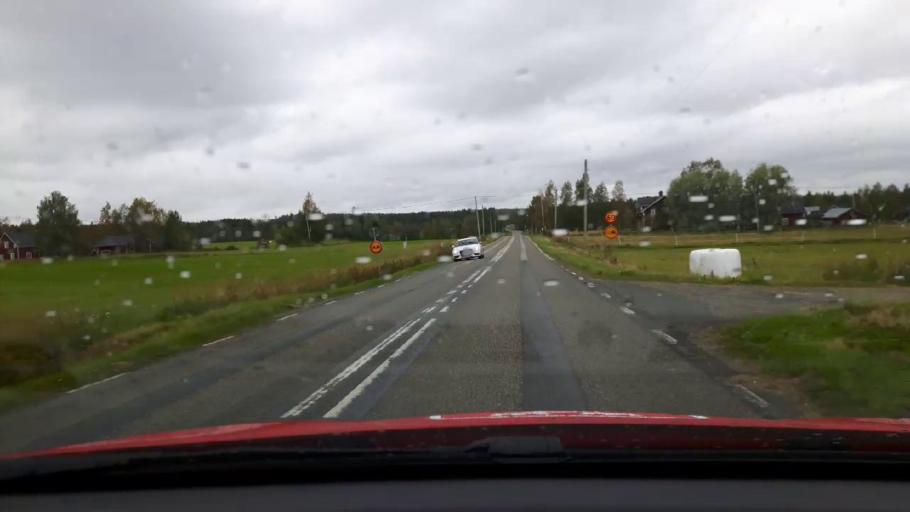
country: SE
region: Jaemtland
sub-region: Bergs Kommun
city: Hoverberg
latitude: 62.8129
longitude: 14.4204
